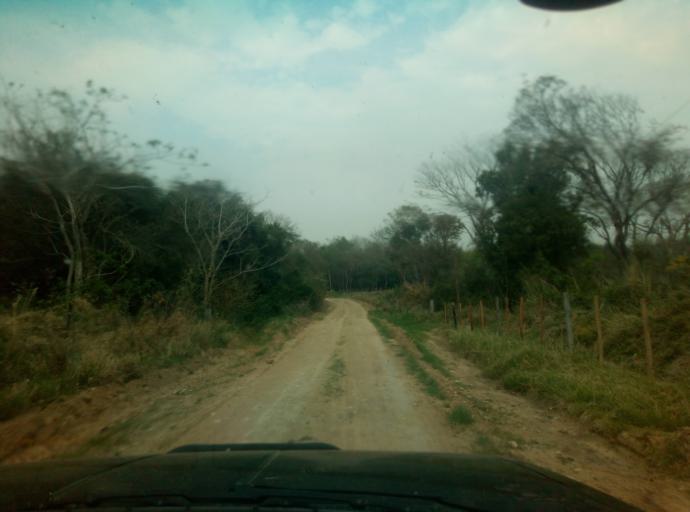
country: PY
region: Caaguazu
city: San Joaquin
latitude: -25.1041
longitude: -56.1300
